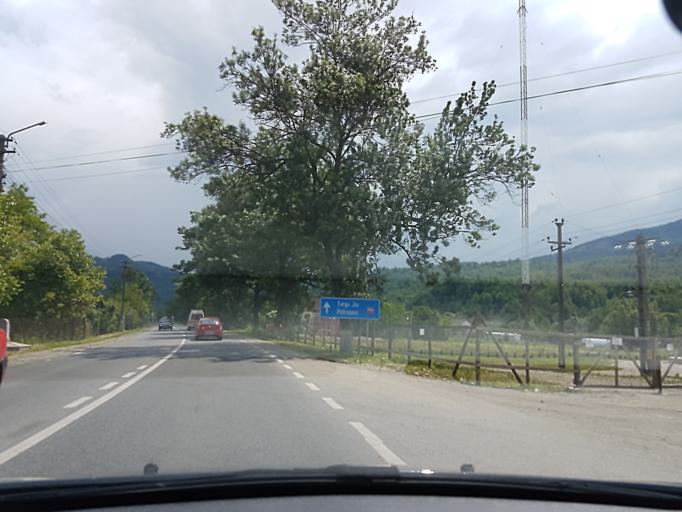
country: RO
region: Hunedoara
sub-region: Comuna Aninoasa
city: Iscroni
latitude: 45.3762
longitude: 23.3422
